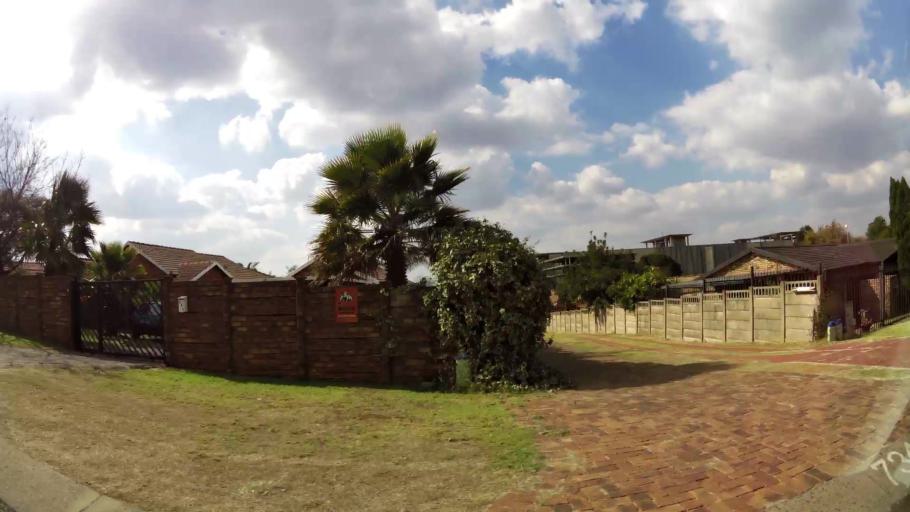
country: ZA
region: Gauteng
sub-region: City of Tshwane Metropolitan Municipality
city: Centurion
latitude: -25.8418
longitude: 28.2718
